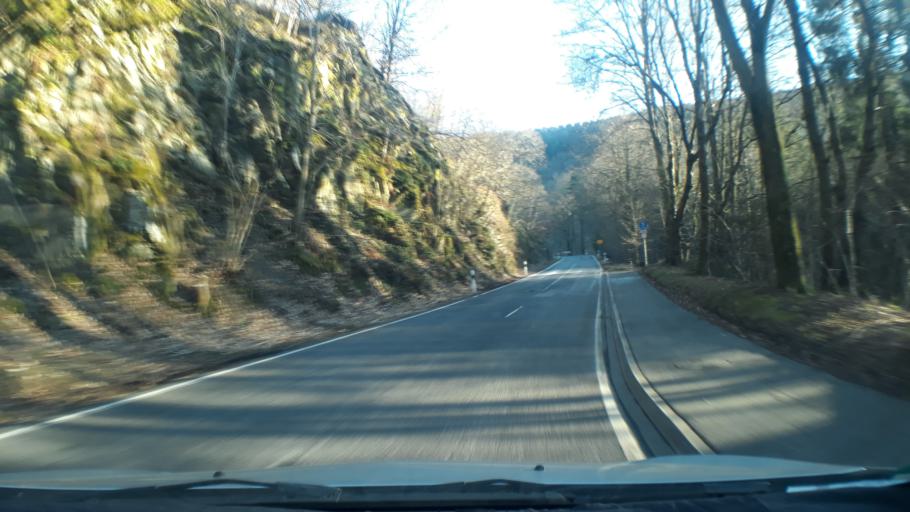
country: DE
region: North Rhine-Westphalia
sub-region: Regierungsbezirk Koln
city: Simmerath
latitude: 50.5620
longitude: 6.3196
